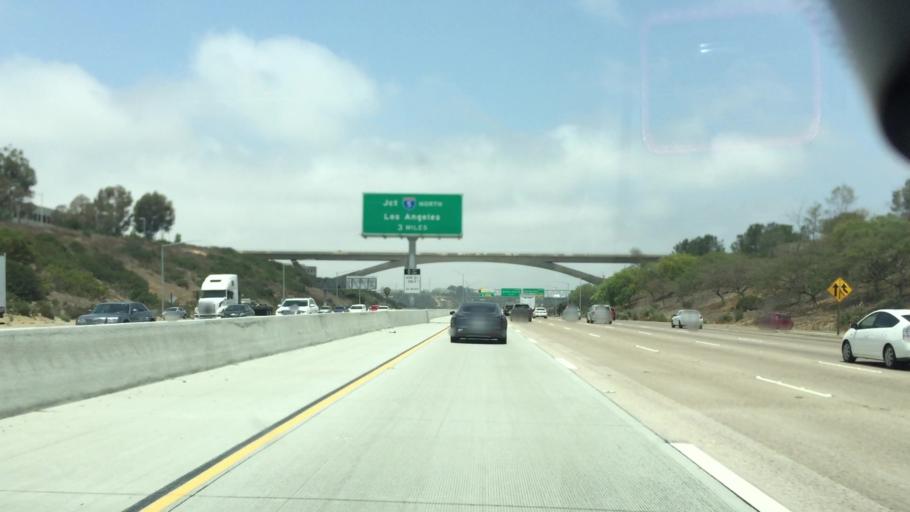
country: US
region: California
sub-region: San Diego County
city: La Jolla
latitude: 32.8780
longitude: -117.2003
